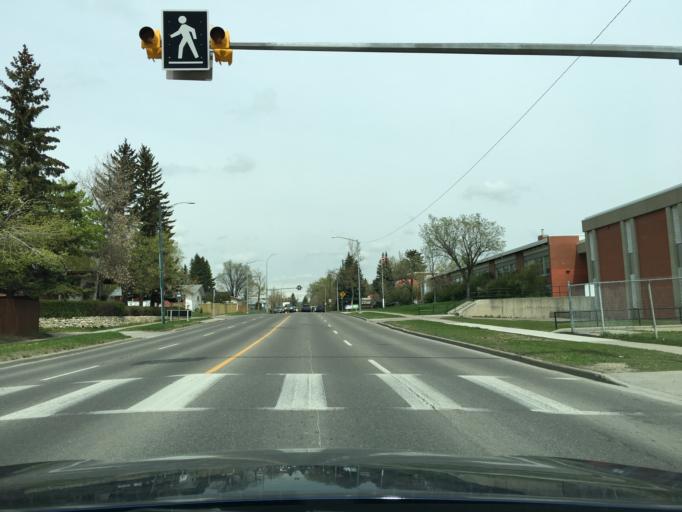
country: CA
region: Alberta
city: Calgary
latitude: 50.9753
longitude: -114.0843
